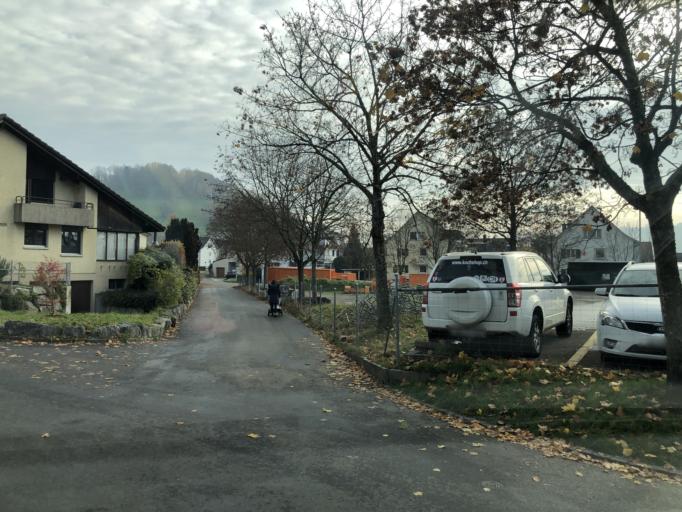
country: CH
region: Aargau
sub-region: Bezirk Baden
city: Wettingen
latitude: 47.4690
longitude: 8.3338
